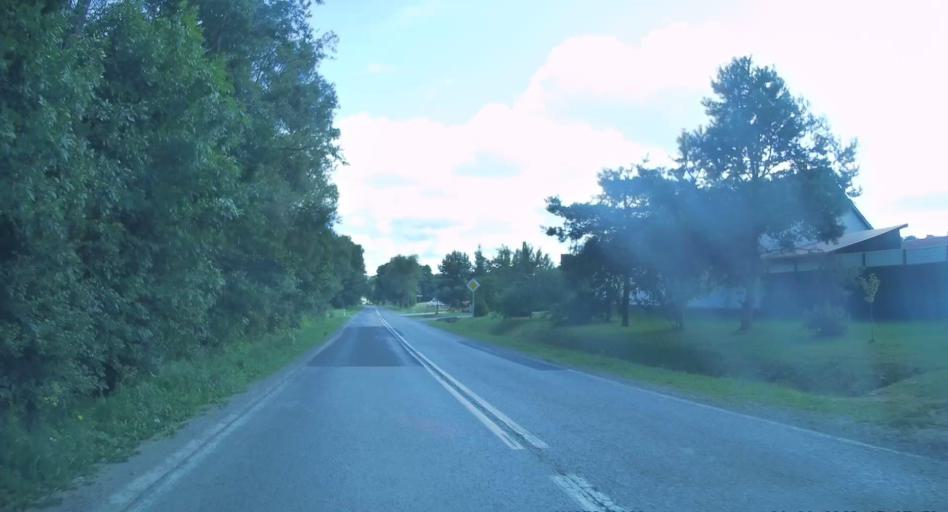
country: PL
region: Swietokrzyskie
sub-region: Powiat kielecki
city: Lagow
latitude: 50.8015
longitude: 21.0811
